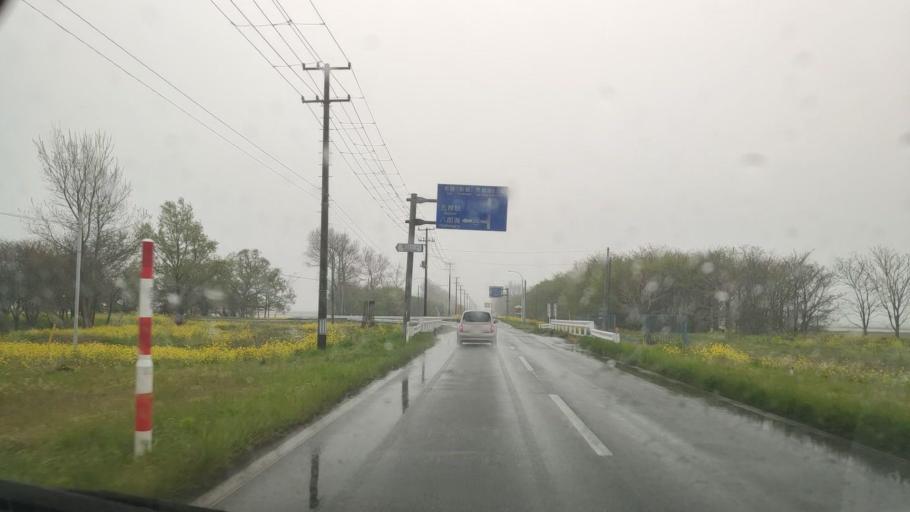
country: JP
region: Akita
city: Tenno
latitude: 39.9923
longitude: 139.9463
